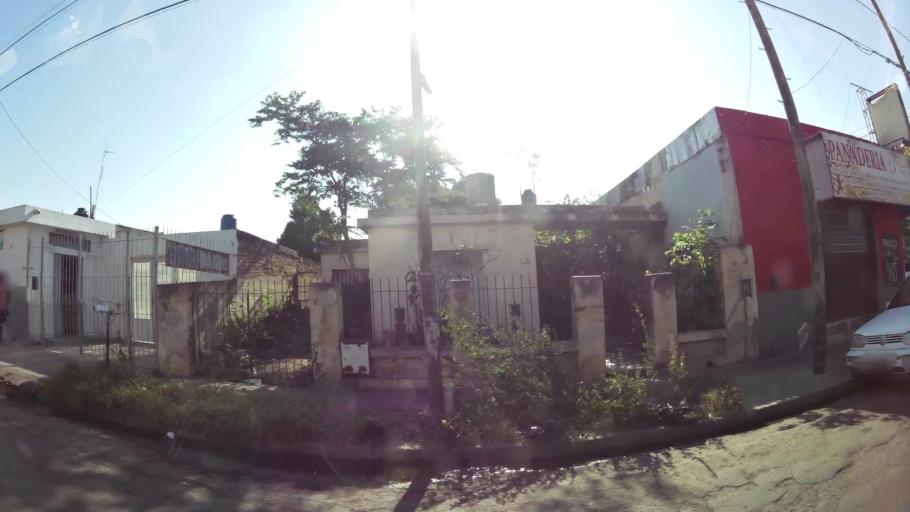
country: AR
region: Cordoba
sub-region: Departamento de Capital
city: Cordoba
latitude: -31.4700
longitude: -64.2240
